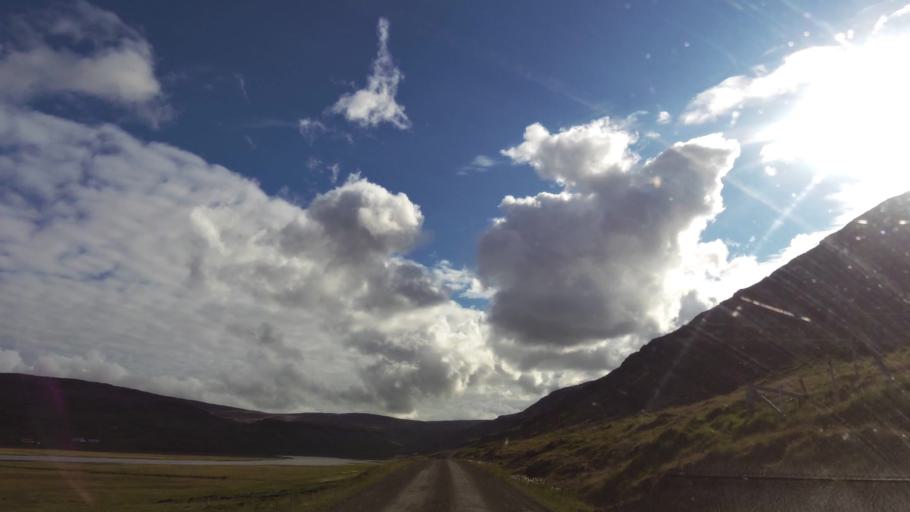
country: IS
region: West
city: Olafsvik
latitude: 65.5757
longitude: -24.1532
